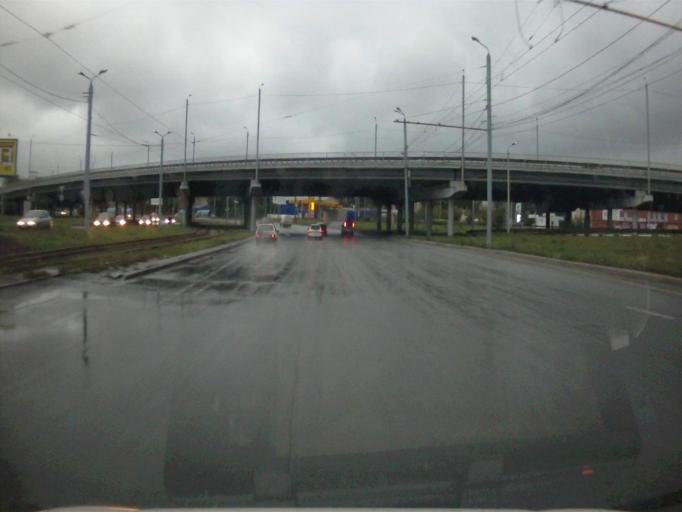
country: RU
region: Chelyabinsk
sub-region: Gorod Chelyabinsk
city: Chelyabinsk
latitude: 55.1515
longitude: 61.4423
